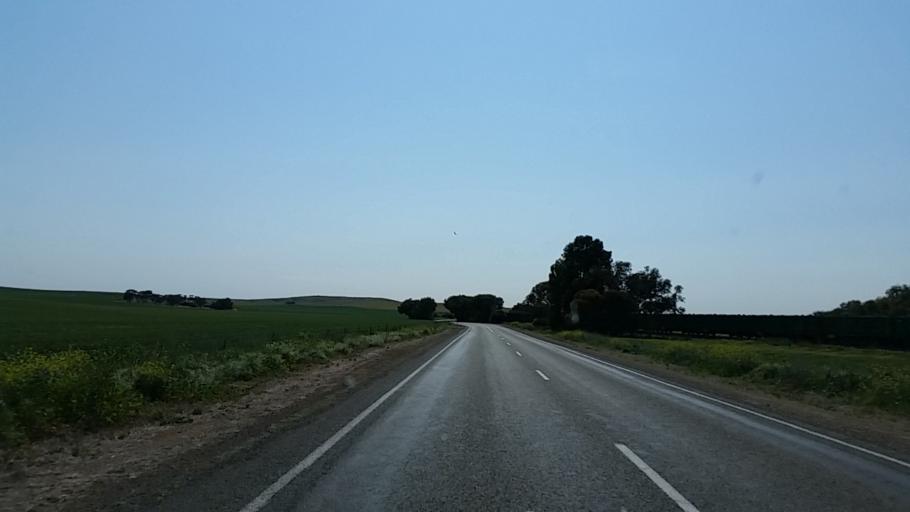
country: AU
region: South Australia
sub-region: Port Pirie City and Dists
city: Crystal Brook
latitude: -33.2526
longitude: 138.3633
